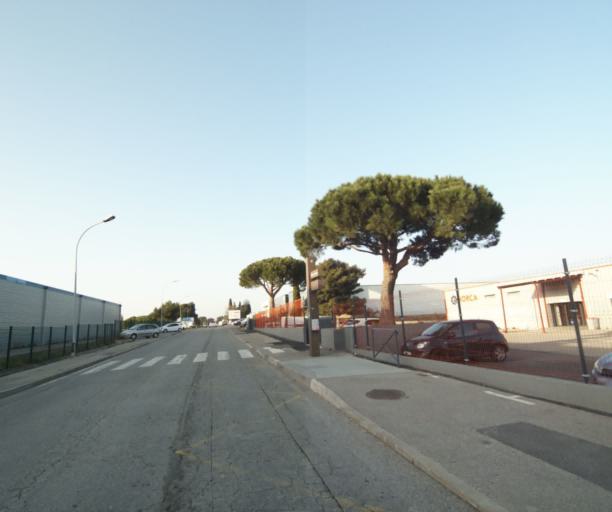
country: FR
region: Provence-Alpes-Cote d'Azur
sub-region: Departement des Bouches-du-Rhone
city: Saint-Victoret
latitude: 43.4343
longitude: 5.2398
